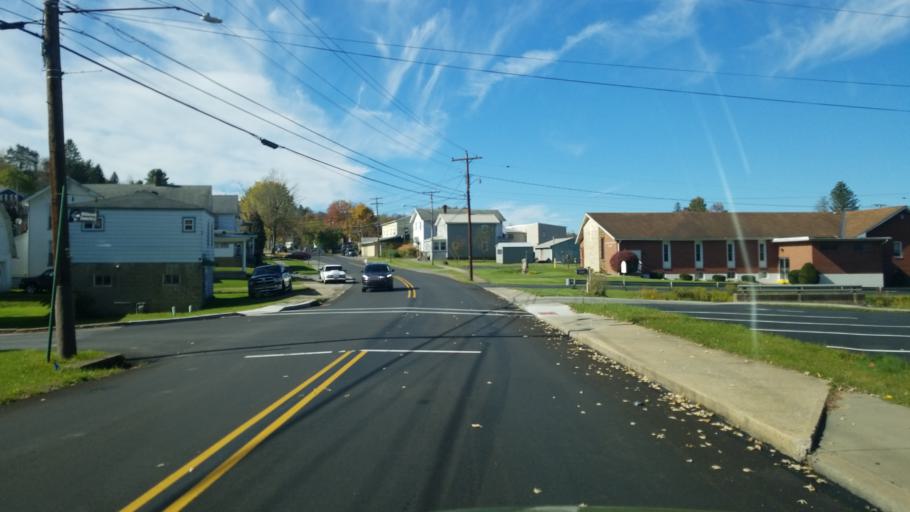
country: US
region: Pennsylvania
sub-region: Jefferson County
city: Brockway
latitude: 41.2471
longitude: -78.7966
